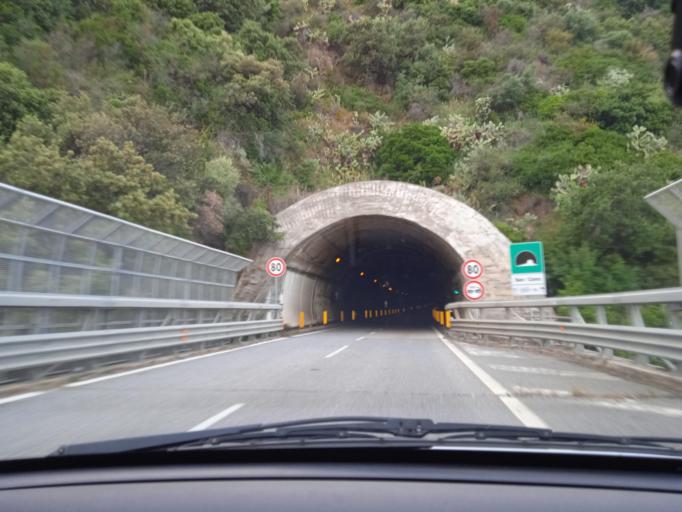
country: IT
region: Sicily
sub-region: Messina
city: Naso
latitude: 38.1461
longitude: 14.7890
